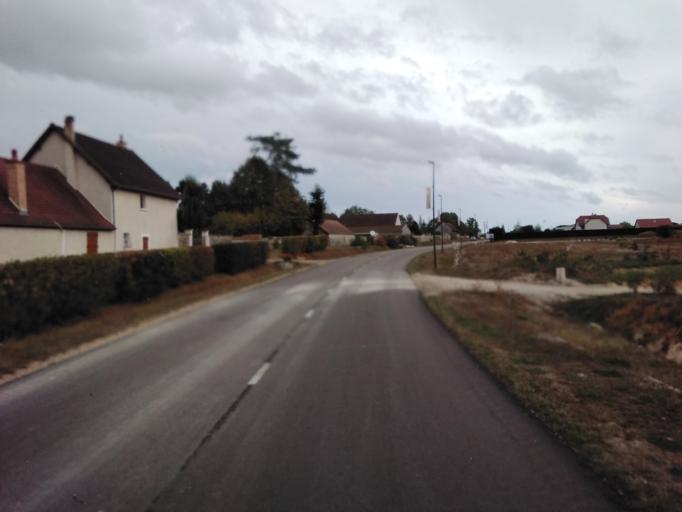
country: FR
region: Champagne-Ardenne
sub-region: Departement de l'Aube
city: Les Riceys
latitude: 47.9875
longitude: 4.3594
